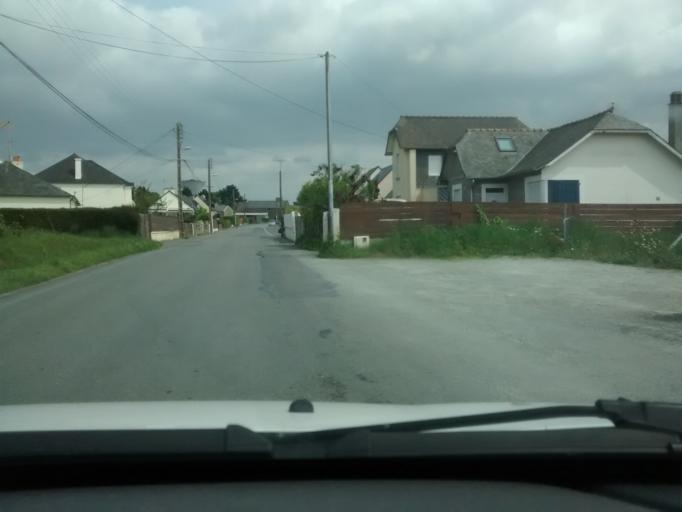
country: FR
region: Brittany
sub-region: Departement d'Ille-et-Vilaine
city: Dinard
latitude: 48.6174
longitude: -2.0630
